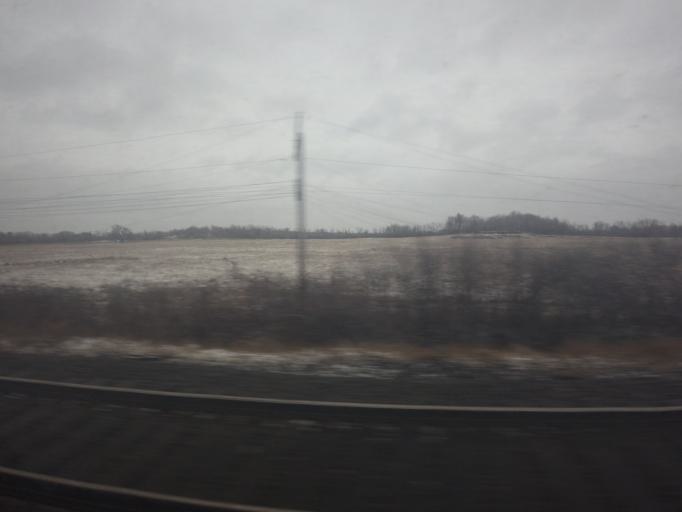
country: CA
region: Ontario
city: Gananoque
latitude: 44.3279
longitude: -76.3238
